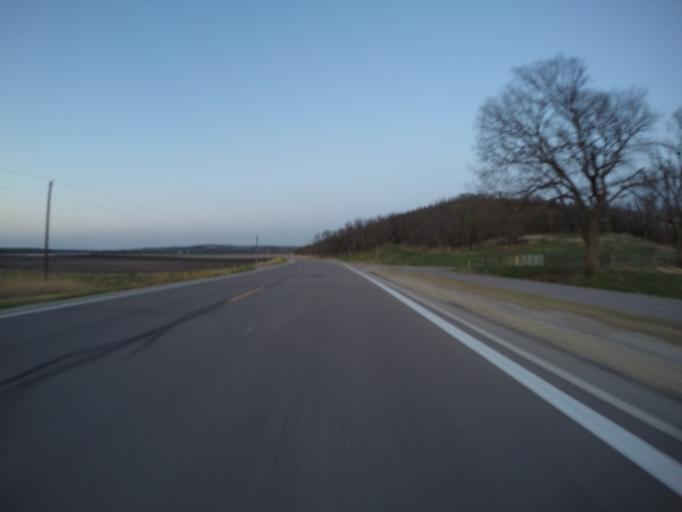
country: US
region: Kansas
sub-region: Riley County
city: Manhattan
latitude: 39.1184
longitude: -96.5792
